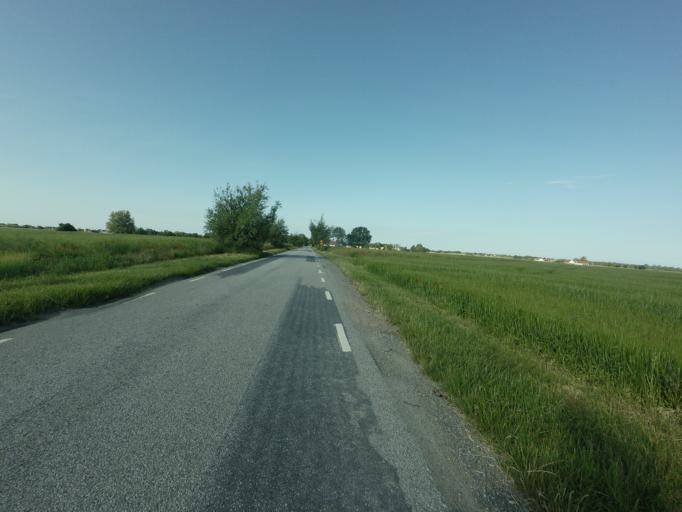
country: SE
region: Skane
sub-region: Trelleborgs Kommun
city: Skare
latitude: 55.4173
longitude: 13.0151
